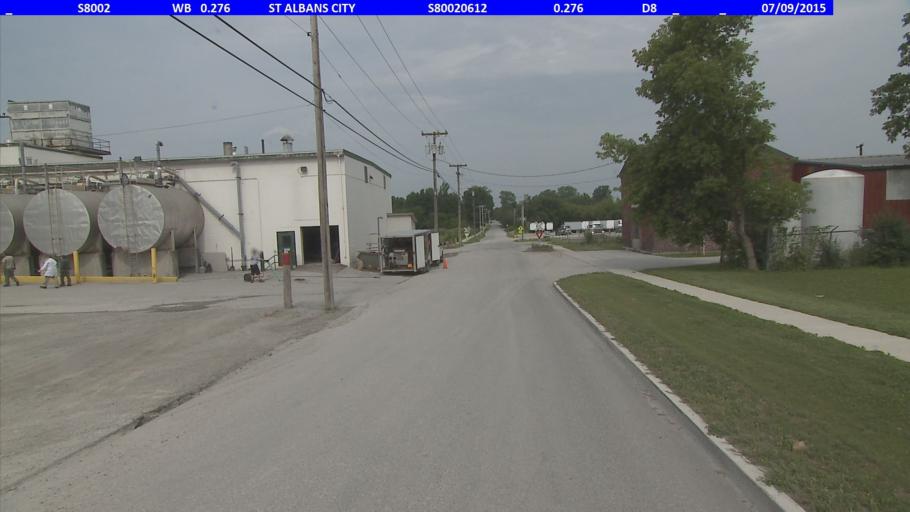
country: US
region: Vermont
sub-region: Franklin County
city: Saint Albans
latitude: 44.8169
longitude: -73.0852
